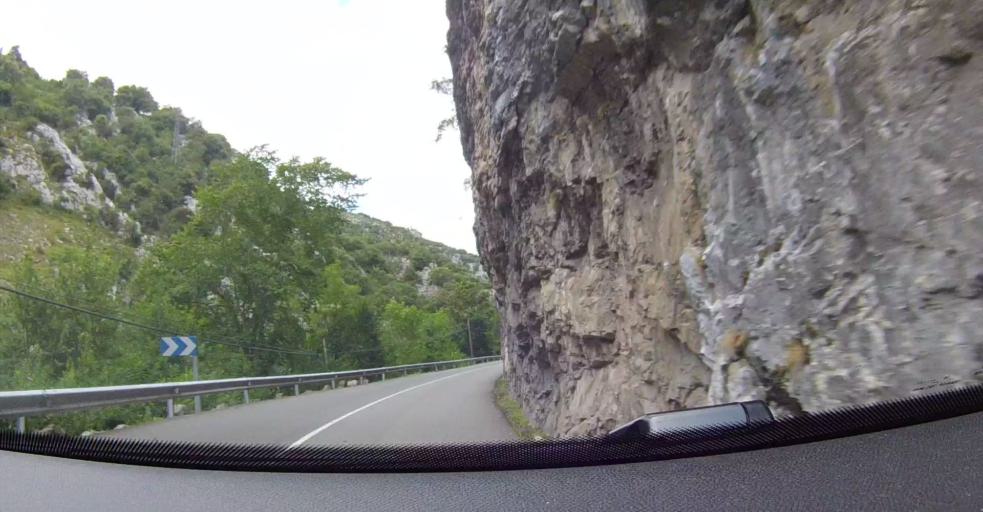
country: ES
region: Cantabria
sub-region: Provincia de Cantabria
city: Tresviso
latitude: 43.3075
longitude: -4.6069
